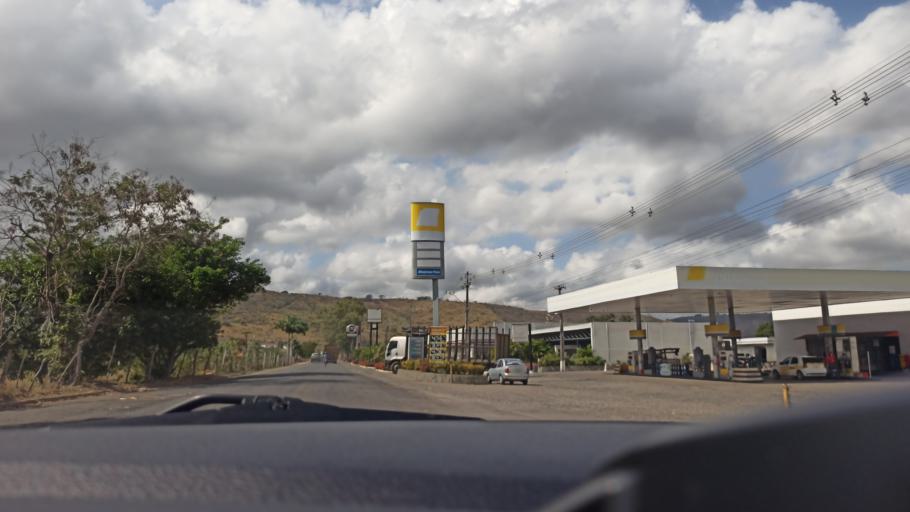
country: BR
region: Pernambuco
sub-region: Timbauba
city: Timbauba
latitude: -7.5135
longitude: -35.3033
